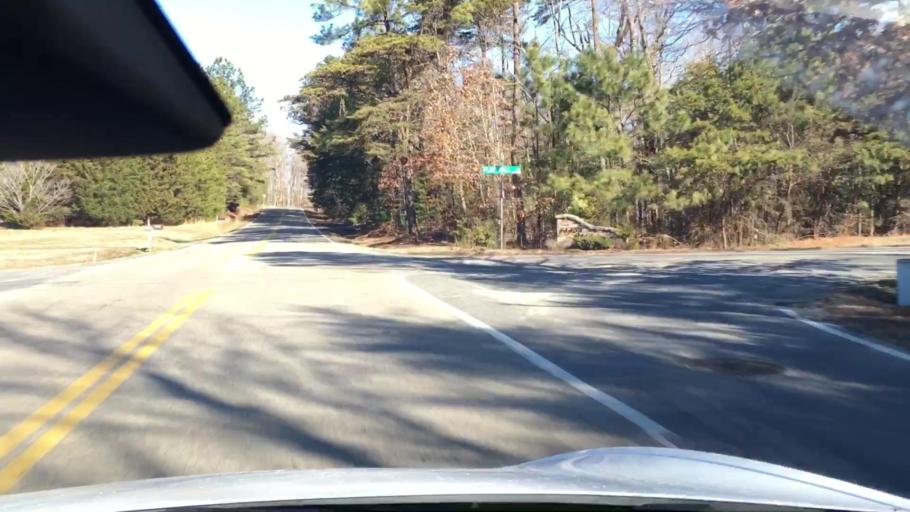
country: US
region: Virginia
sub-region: Powhatan County
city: Powhatan
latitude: 37.5385
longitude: -77.7981
